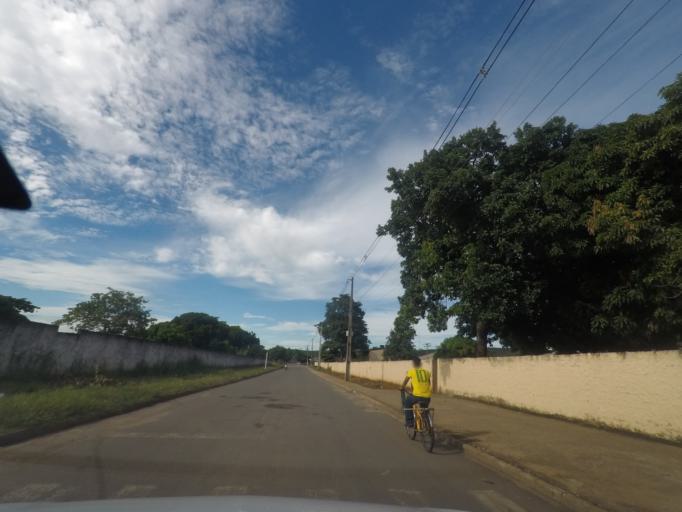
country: BR
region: Goias
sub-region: Aparecida De Goiania
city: Aparecida de Goiania
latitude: -16.8252
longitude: -49.2968
